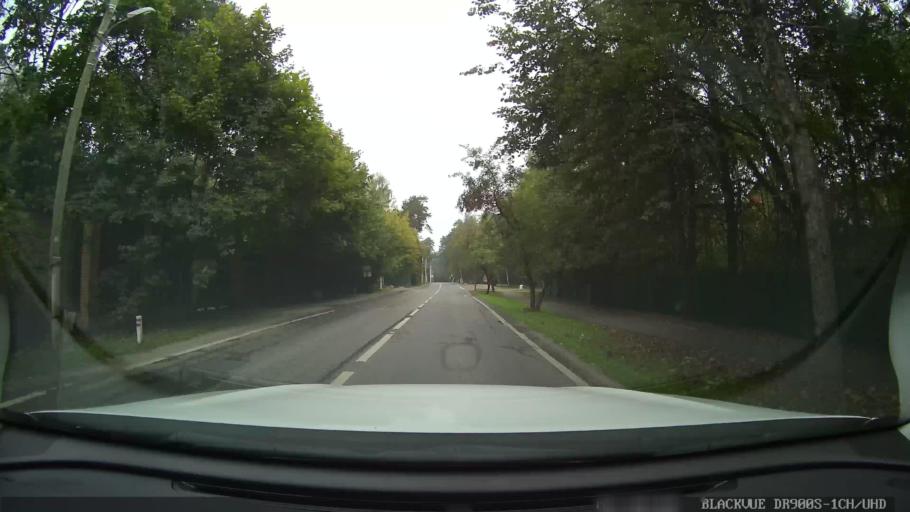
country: RU
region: Moscow
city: Novo-Peredelkino
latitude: 55.6494
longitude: 37.3588
